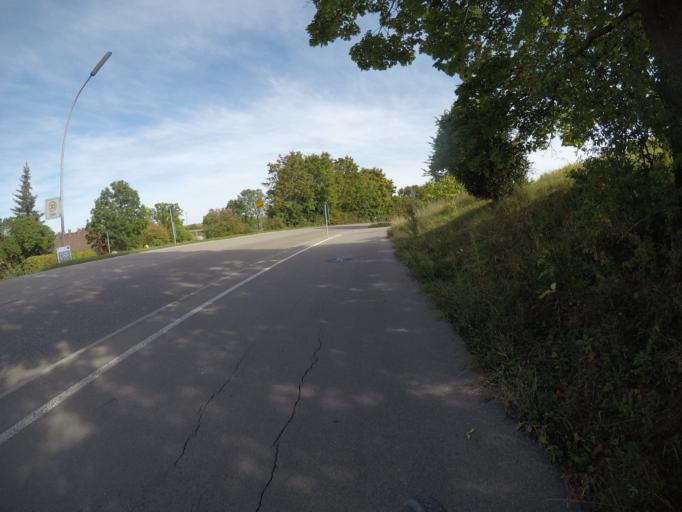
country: DE
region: Baden-Wuerttemberg
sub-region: Regierungsbezirk Stuttgart
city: Schwieberdingen
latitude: 48.8593
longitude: 9.0909
